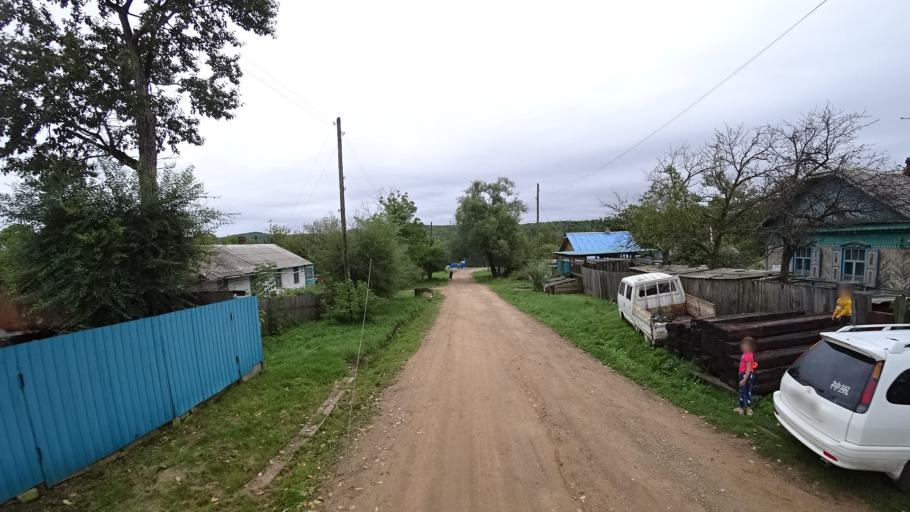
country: RU
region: Primorskiy
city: Rettikhovka
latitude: 44.1684
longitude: 132.7685
